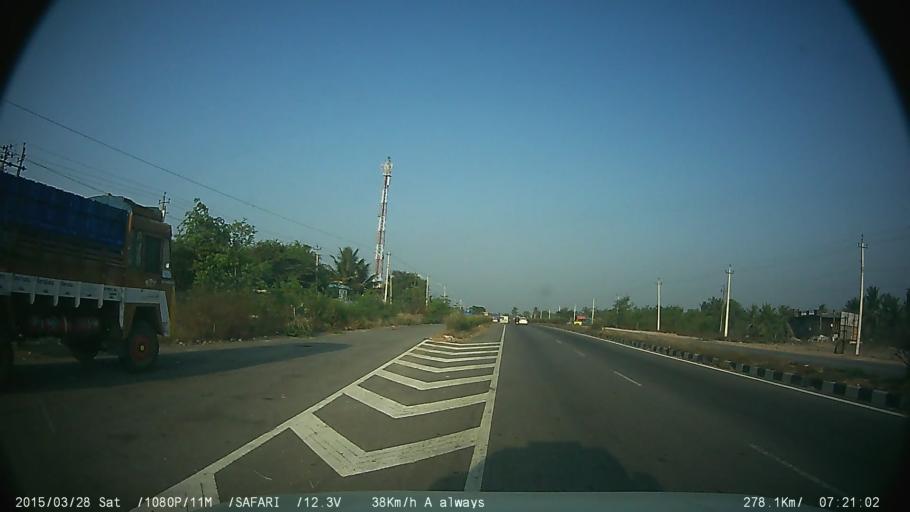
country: IN
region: Karnataka
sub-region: Mandya
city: Mandya
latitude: 12.4965
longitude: 76.8072
